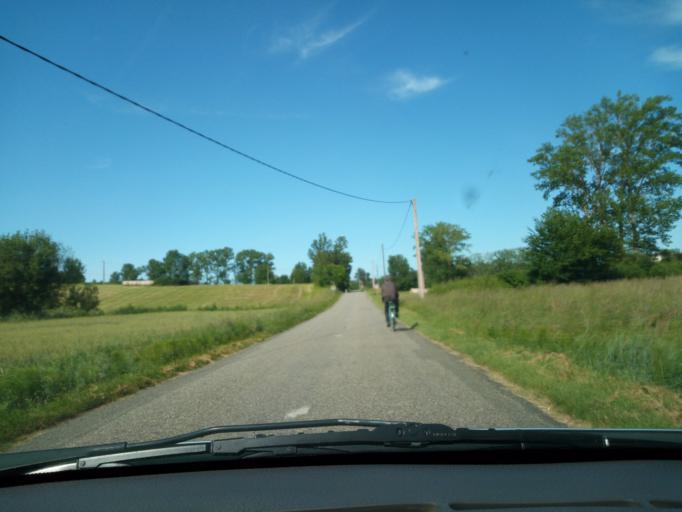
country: FR
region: Midi-Pyrenees
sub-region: Departement du Tarn-et-Garonne
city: Molieres
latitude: 44.2069
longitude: 1.3074
